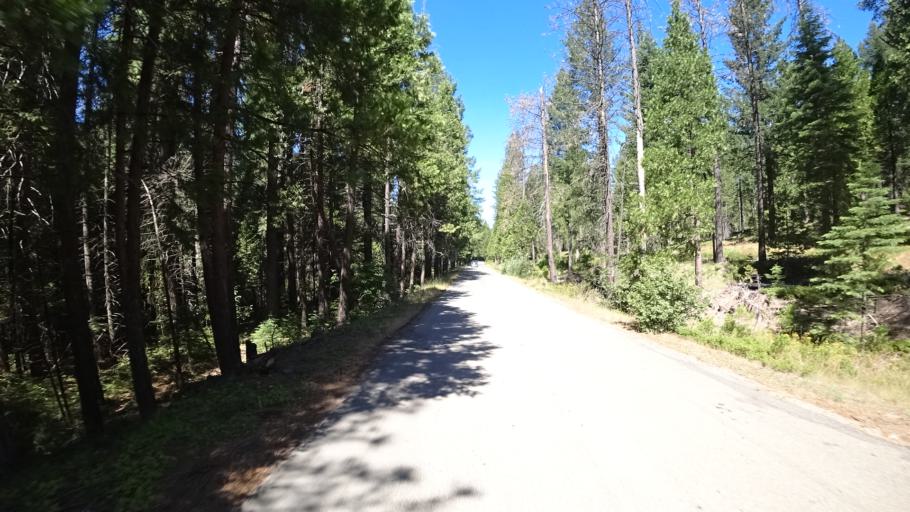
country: US
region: California
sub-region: Amador County
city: Pioneer
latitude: 38.4297
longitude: -120.4541
